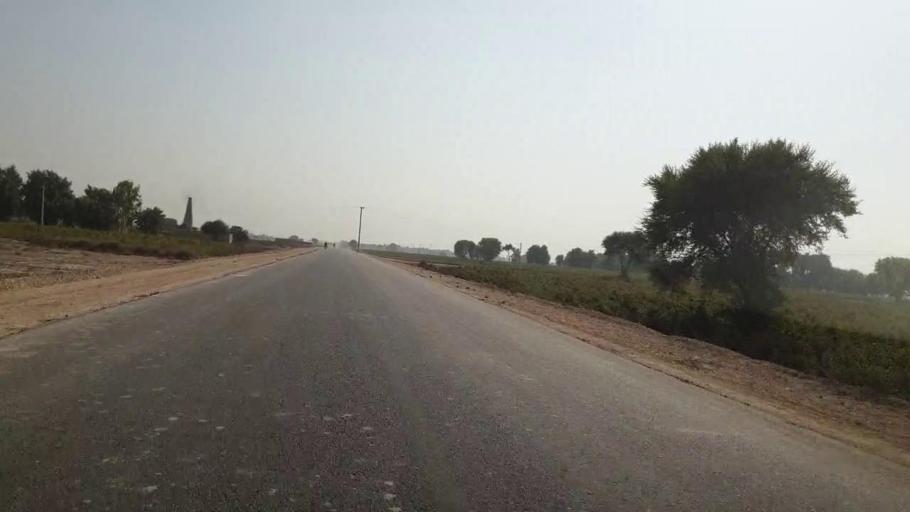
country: PK
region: Sindh
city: Dadu
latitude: 26.6624
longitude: 67.7764
